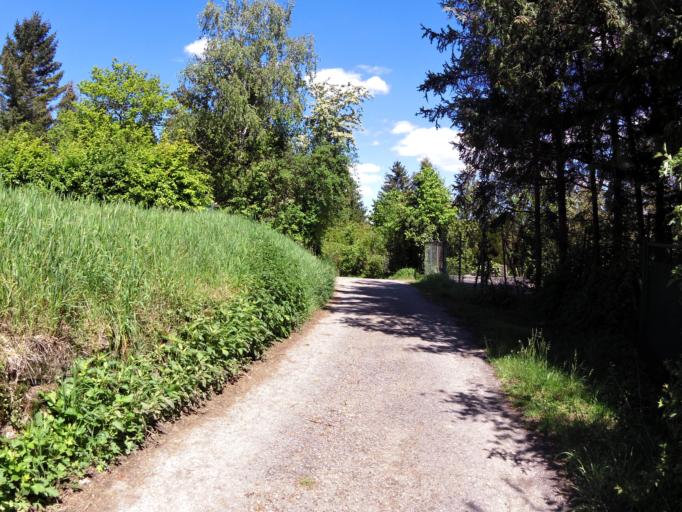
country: DE
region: Bavaria
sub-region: Regierungsbezirk Unterfranken
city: Reichenberg
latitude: 49.7482
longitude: 9.9334
